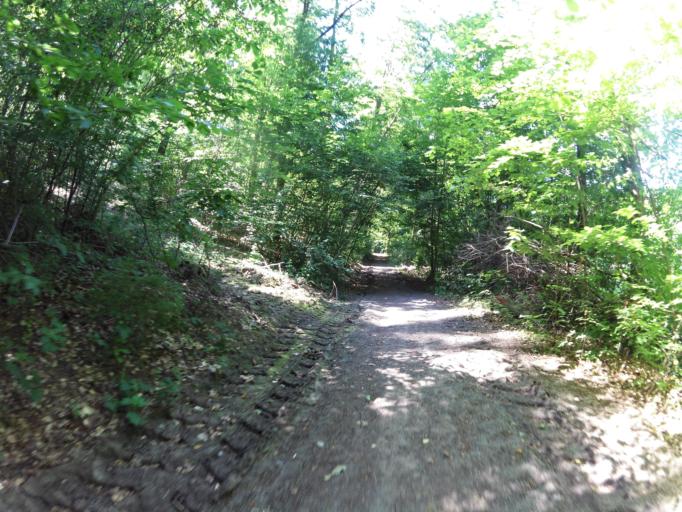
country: DE
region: Bavaria
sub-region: Regierungsbezirk Unterfranken
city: Zellingen
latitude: 49.9036
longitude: 9.8411
